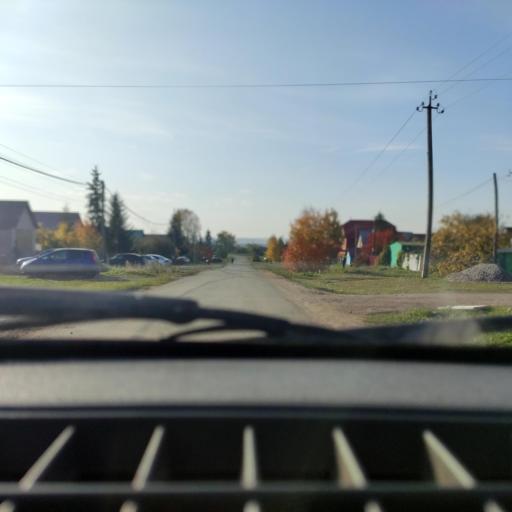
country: RU
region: Bashkortostan
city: Avdon
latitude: 54.6572
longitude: 55.7704
